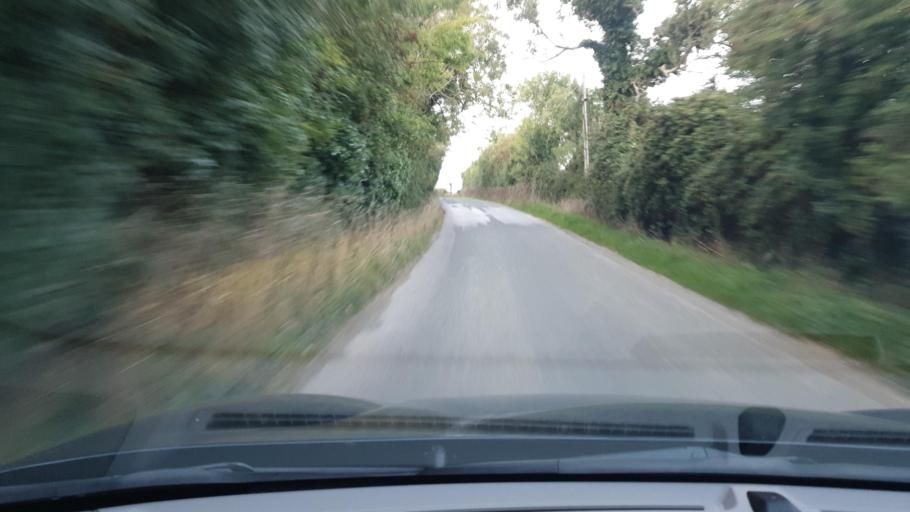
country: IE
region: Leinster
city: Balrothery
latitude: 53.5696
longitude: -6.1646
